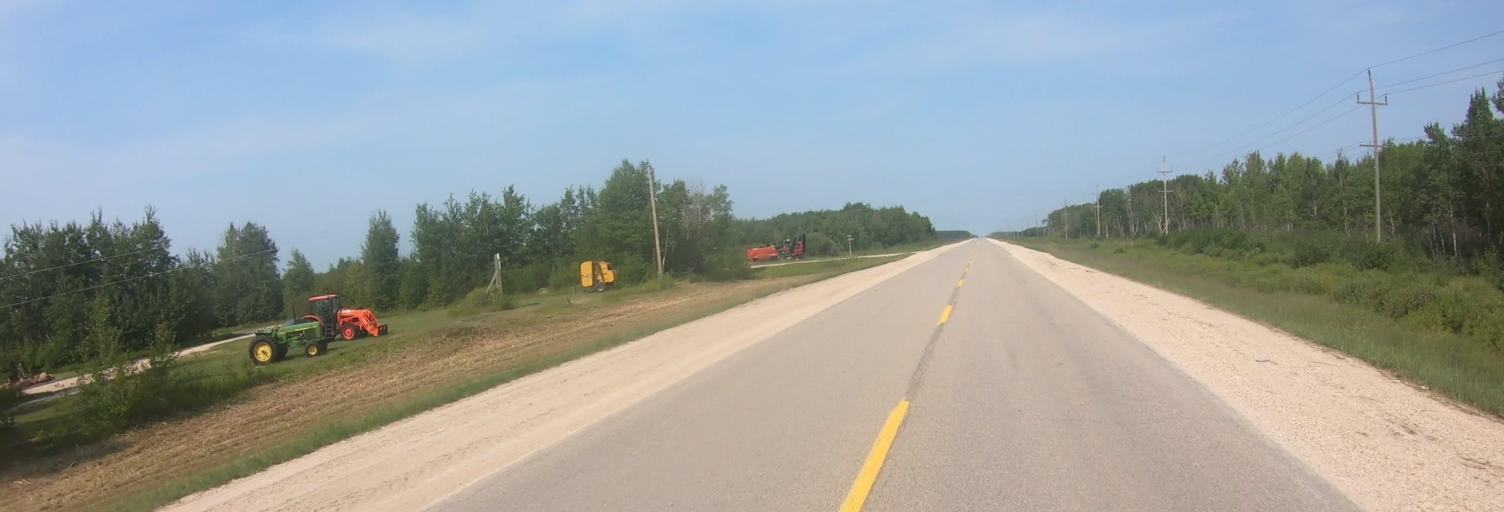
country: CA
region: Manitoba
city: La Broquerie
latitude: 49.2941
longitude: -96.5319
